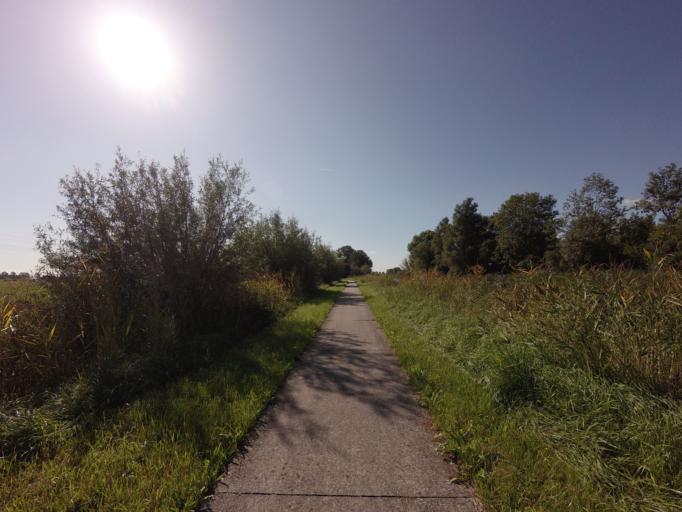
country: NL
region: Friesland
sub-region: Gemeente Leeuwarden
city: Wirdum
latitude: 53.1579
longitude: 5.7656
